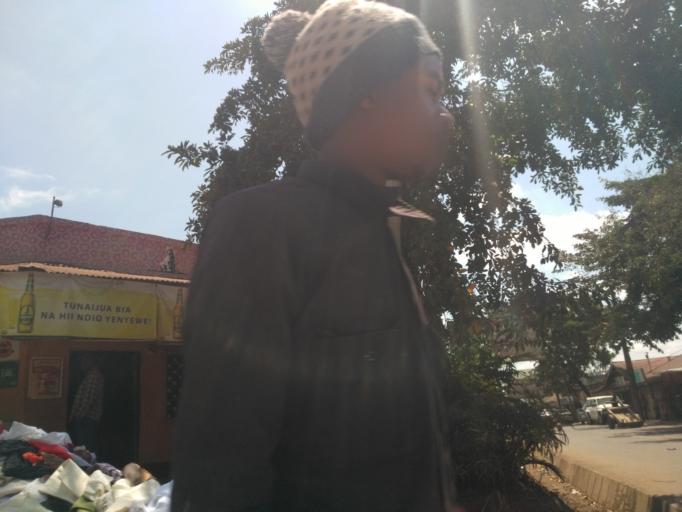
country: TZ
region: Arusha
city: Arusha
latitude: -3.3664
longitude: 36.6853
